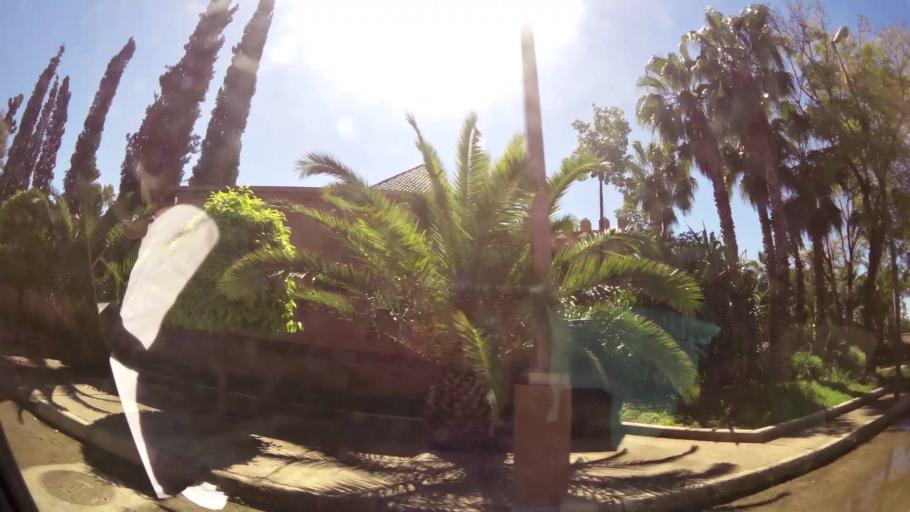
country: MA
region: Marrakech-Tensift-Al Haouz
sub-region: Marrakech
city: Marrakesh
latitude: 31.6597
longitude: -7.9617
